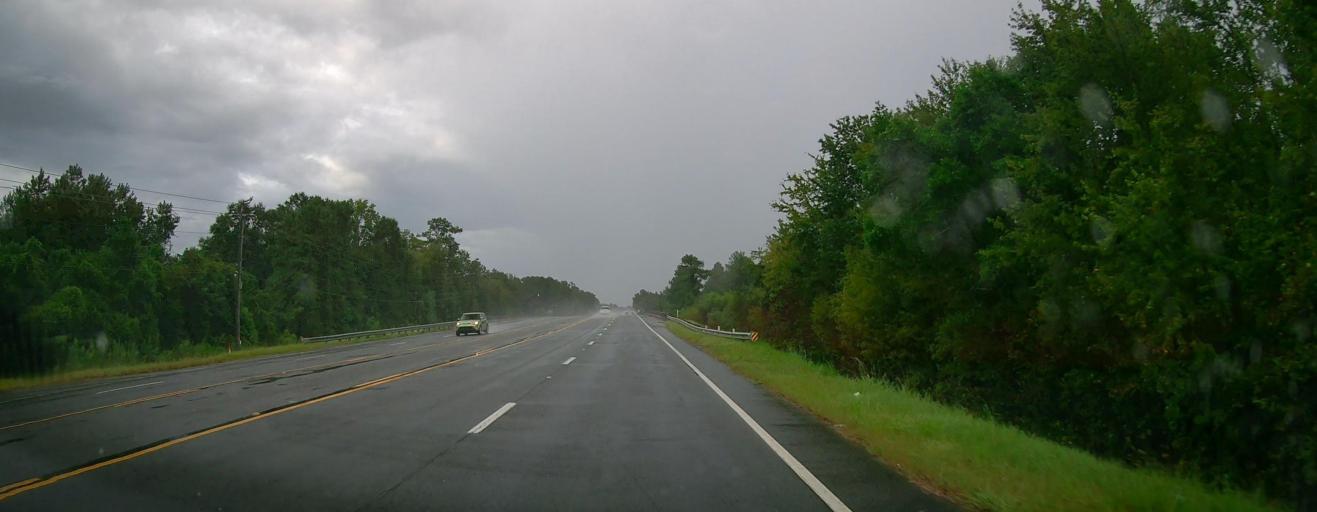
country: US
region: Georgia
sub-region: Ware County
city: Sunnyside
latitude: 31.2349
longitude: -82.3270
